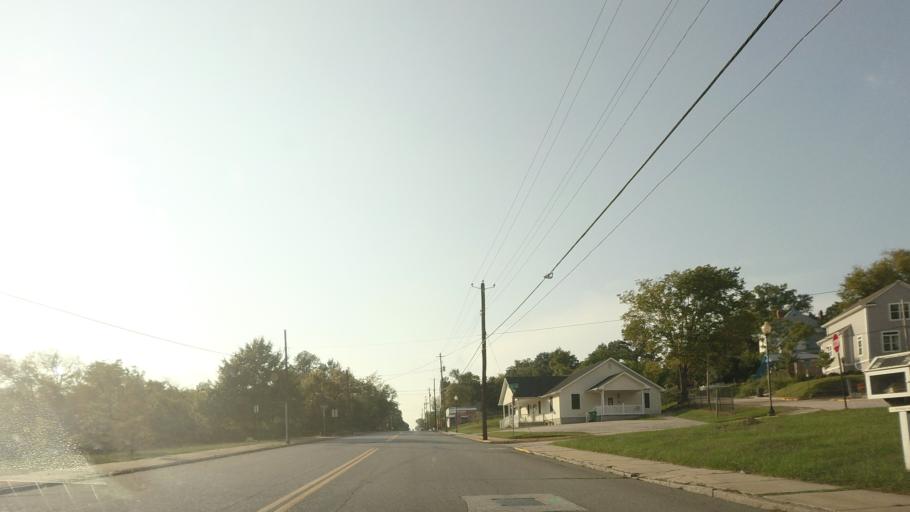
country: US
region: Georgia
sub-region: Bibb County
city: Macon
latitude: 32.8305
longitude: -83.6394
